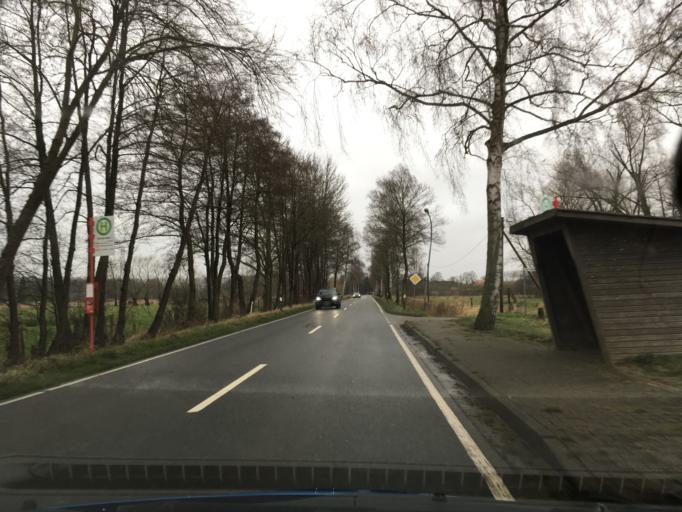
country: DE
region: Lower Saxony
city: Neetze
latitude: 53.3106
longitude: 10.6683
